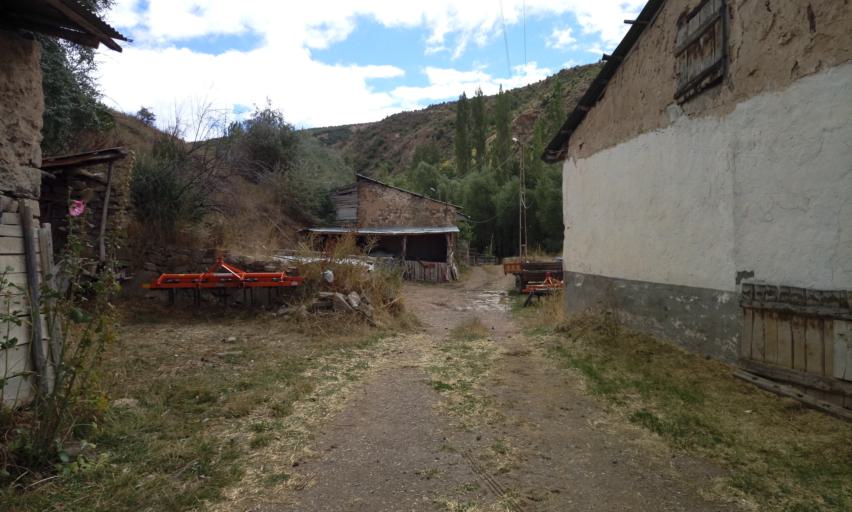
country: TR
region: Sivas
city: Zara
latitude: 39.8276
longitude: 37.9032
